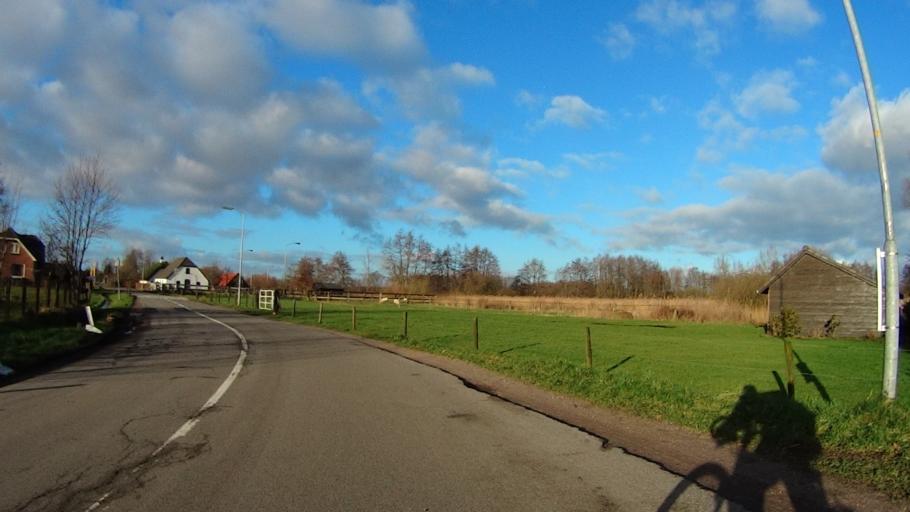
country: NL
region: Gelderland
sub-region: Gemeente Barneveld
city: Zwartebroek
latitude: 52.1814
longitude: 5.5011
